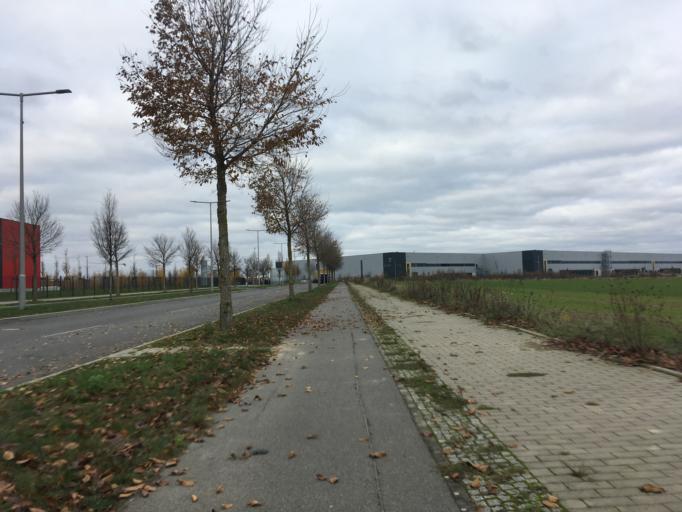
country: DE
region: Berlin
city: Altglienicke
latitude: 52.3899
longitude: 13.5472
